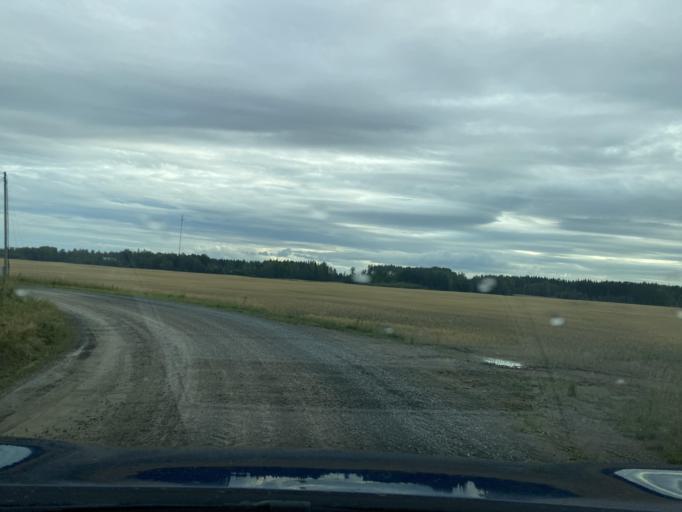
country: FI
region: Pirkanmaa
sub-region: Lounais-Pirkanmaa
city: Punkalaidun
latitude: 61.2197
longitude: 23.0325
